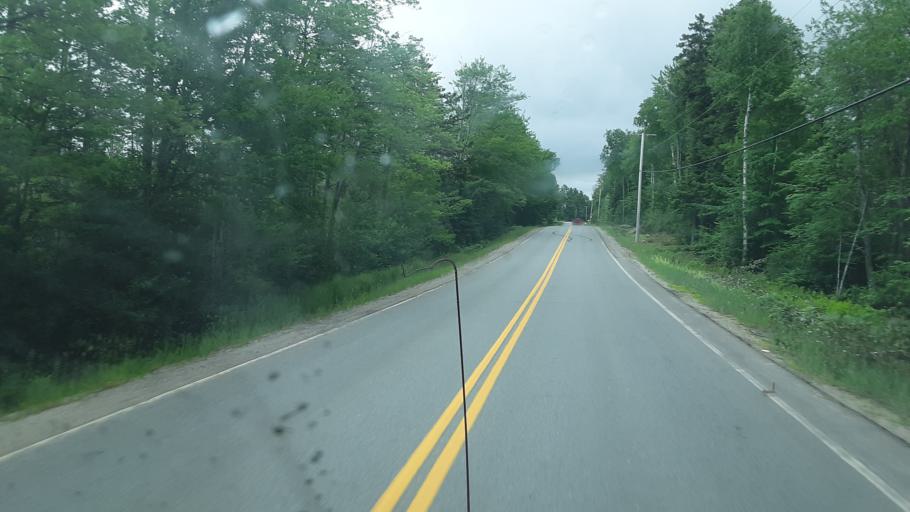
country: US
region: Maine
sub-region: Penobscot County
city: Millinocket
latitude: 45.6825
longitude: -68.7658
